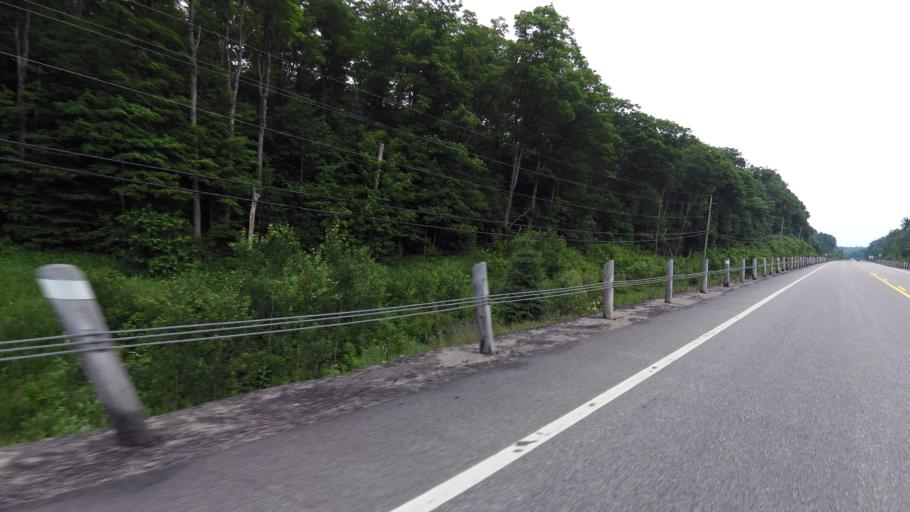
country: CA
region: Ontario
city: Huntsville
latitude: 45.3457
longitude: -78.9396
